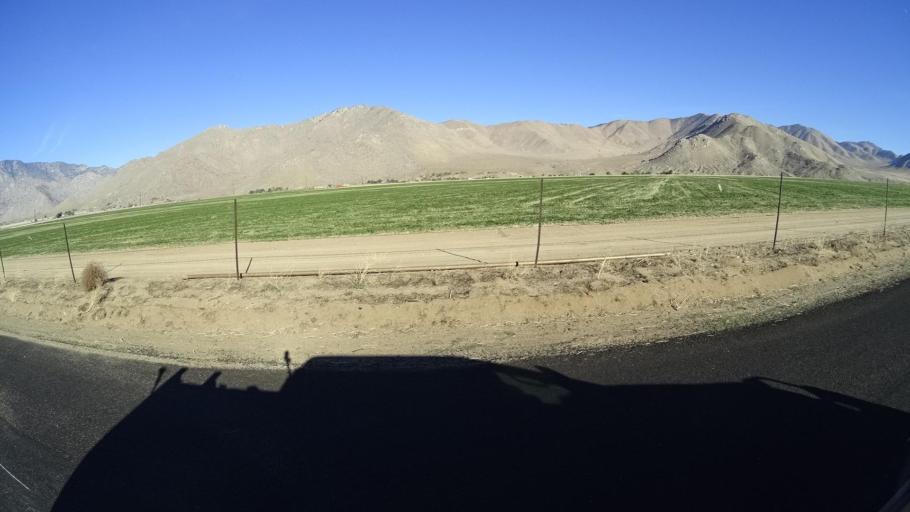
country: US
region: California
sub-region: Kern County
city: Weldon
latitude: 35.6348
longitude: -118.2662
